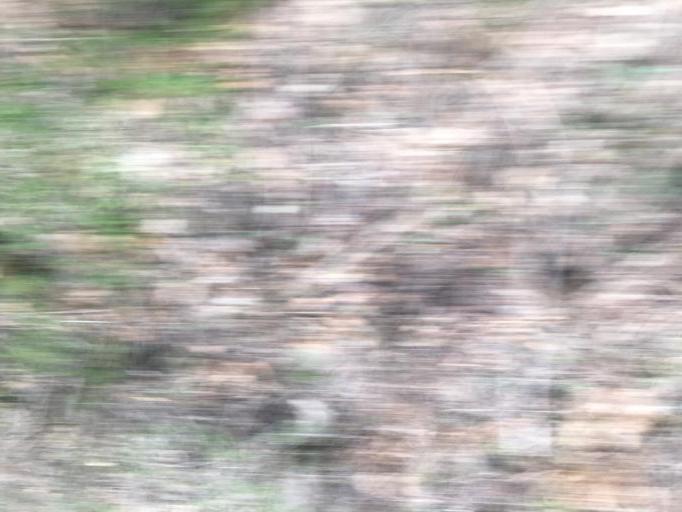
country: JP
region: Aomori
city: Shimokizukuri
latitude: 40.7780
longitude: 140.1921
